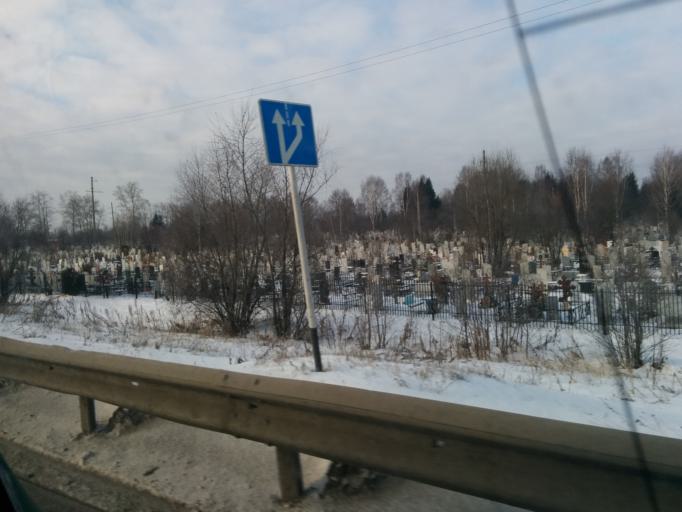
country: RU
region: Perm
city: Ust'-Kachka
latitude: 58.0790
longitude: 55.6593
